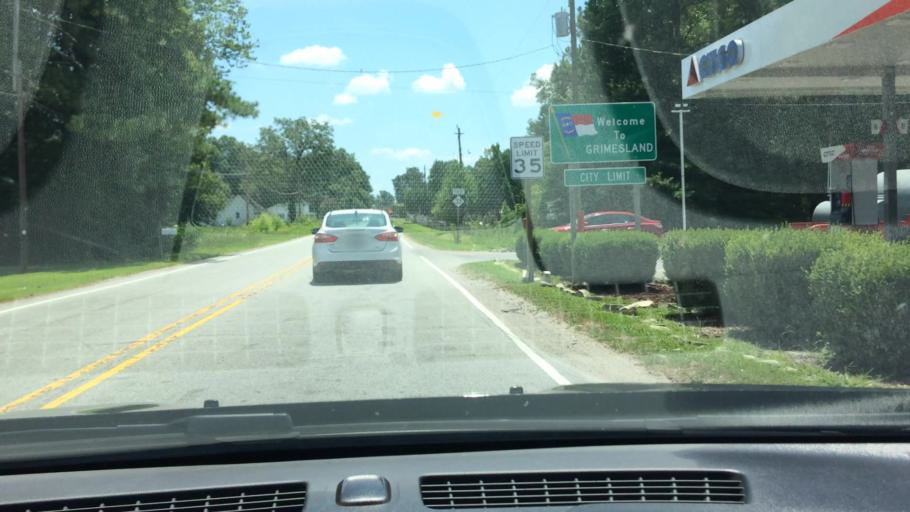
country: US
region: North Carolina
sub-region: Beaufort County
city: Washington
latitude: 35.5677
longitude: -77.2002
